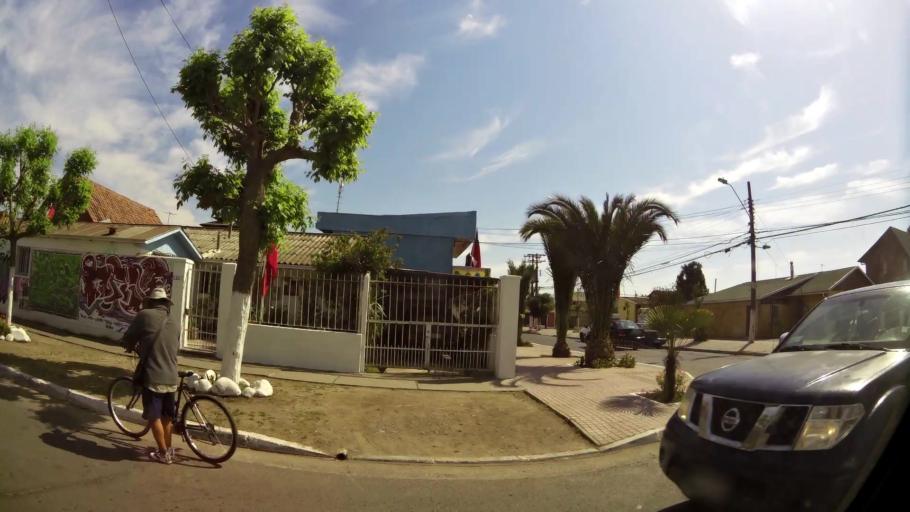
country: CL
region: Santiago Metropolitan
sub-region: Provincia de Talagante
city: Talagante
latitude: -33.6676
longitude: -70.9248
